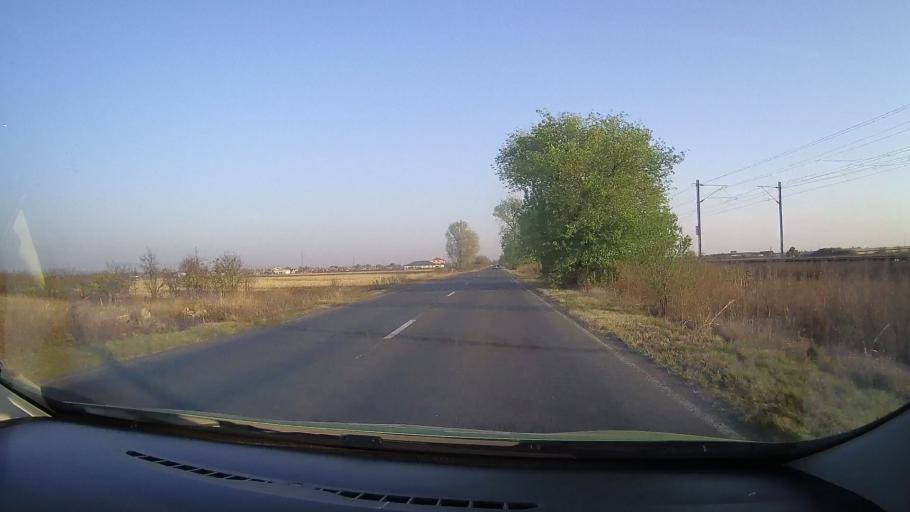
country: RO
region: Arad
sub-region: Comuna Sofronea
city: Sofronea
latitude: 46.2669
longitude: 21.3162
